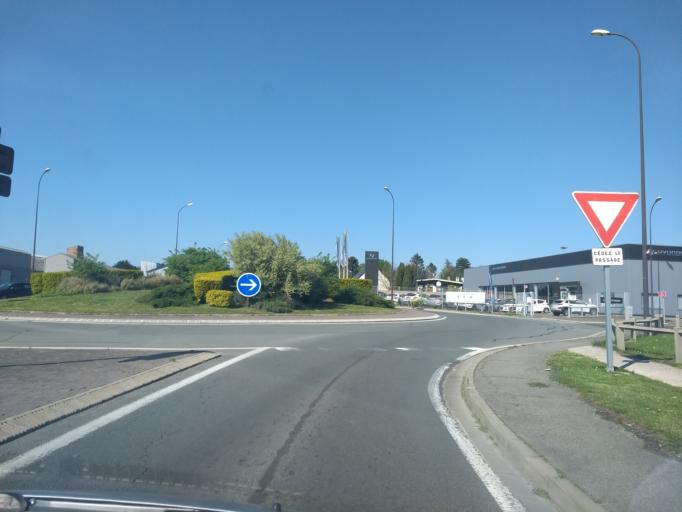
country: FR
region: Picardie
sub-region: Departement de la Somme
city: Poulainville
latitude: 49.9556
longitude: 2.3112
